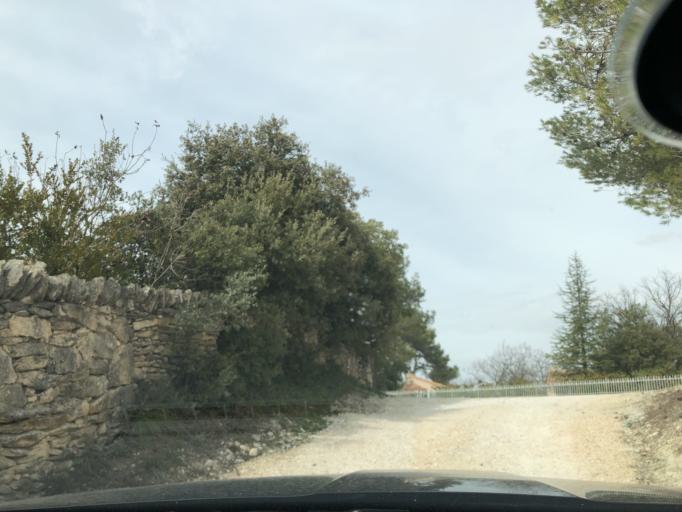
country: FR
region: Provence-Alpes-Cote d'Azur
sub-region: Departement du Vaucluse
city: Goult
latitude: 43.8272
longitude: 5.2446
